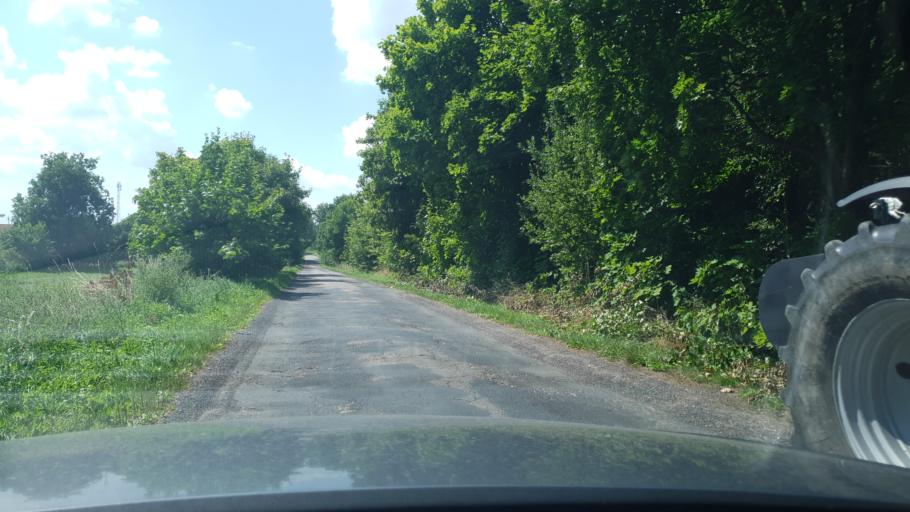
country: PL
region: Kujawsko-Pomorskie
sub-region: Powiat wabrzeski
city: Pluznica
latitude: 53.3212
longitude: 18.8292
